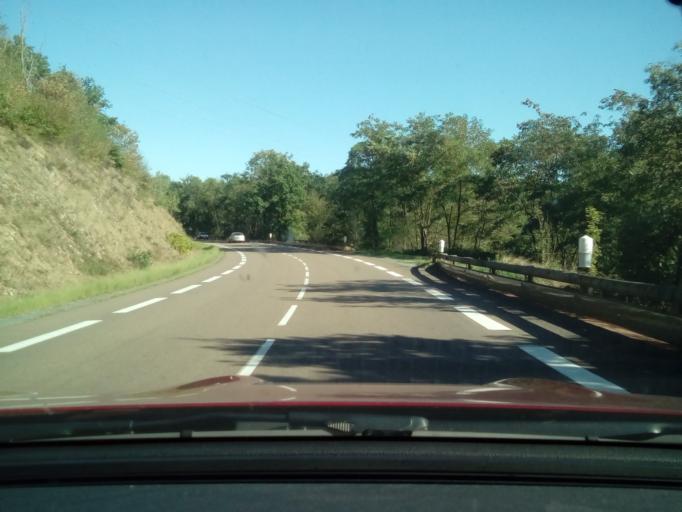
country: FR
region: Rhone-Alpes
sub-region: Departement du Rhone
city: Saint-Verand
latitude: 45.9134
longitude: 4.4962
